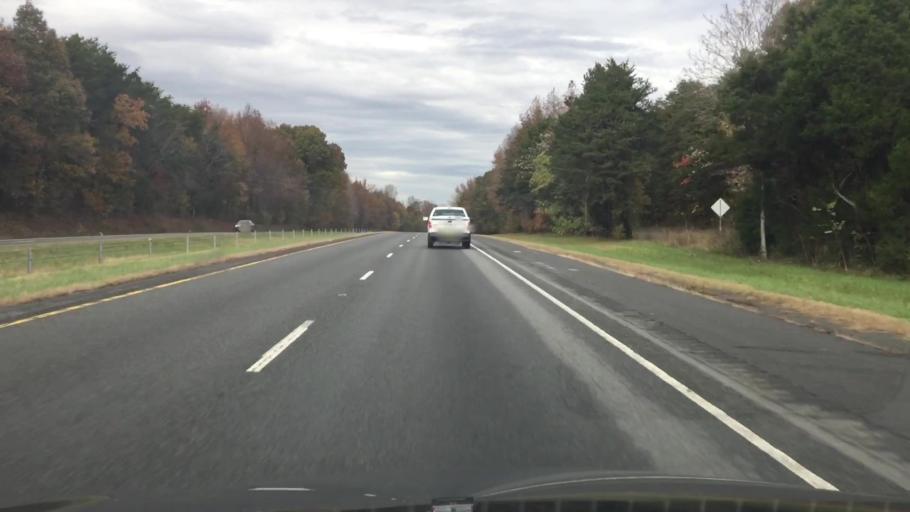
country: US
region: North Carolina
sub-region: Rockingham County
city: Reidsville
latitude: 36.2884
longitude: -79.6410
